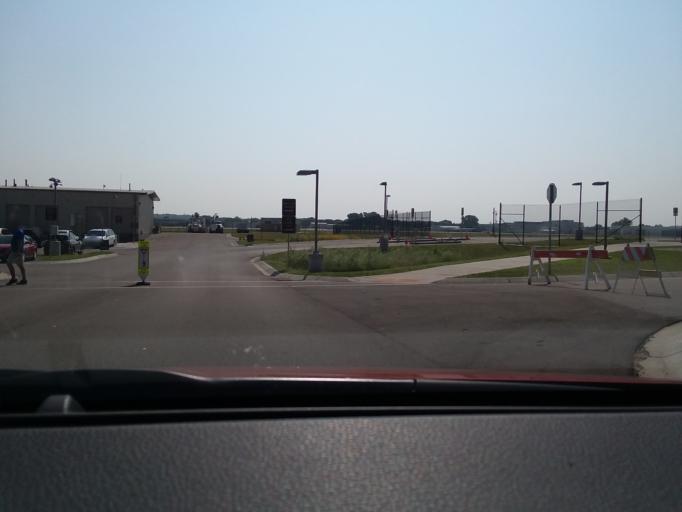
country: US
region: Wisconsin
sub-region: Dane County
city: Maple Bluff
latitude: 43.1316
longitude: -89.3471
